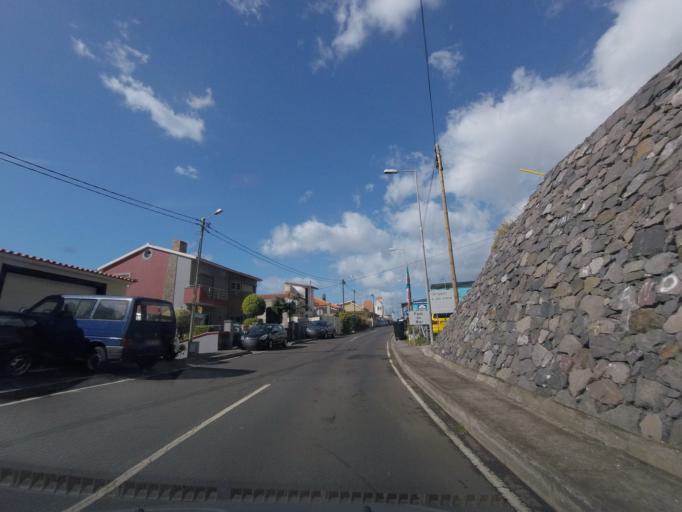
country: PT
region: Madeira
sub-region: Calheta
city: Faja da Ovelha
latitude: 32.7534
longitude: -17.2246
